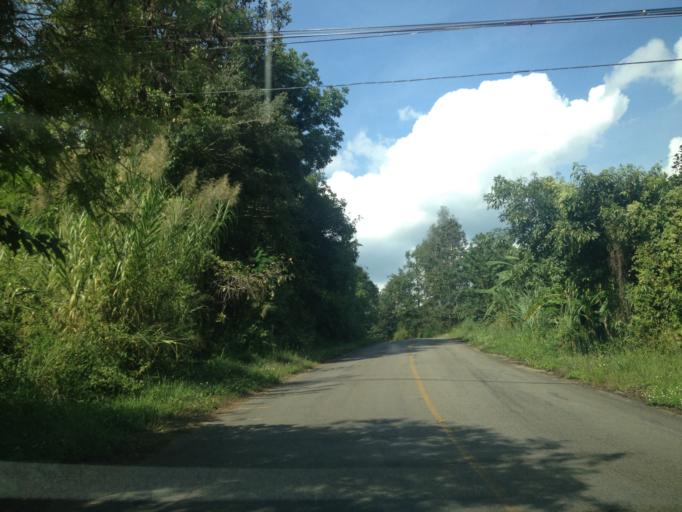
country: TH
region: Chiang Mai
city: Samoeng
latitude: 18.8084
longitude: 98.8188
